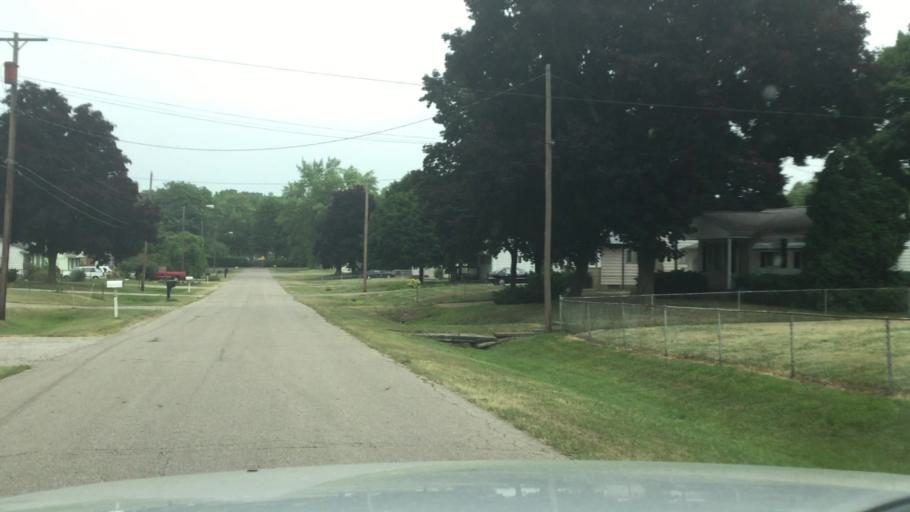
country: US
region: Michigan
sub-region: Genesee County
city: Flint
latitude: 42.9607
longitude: -83.7018
